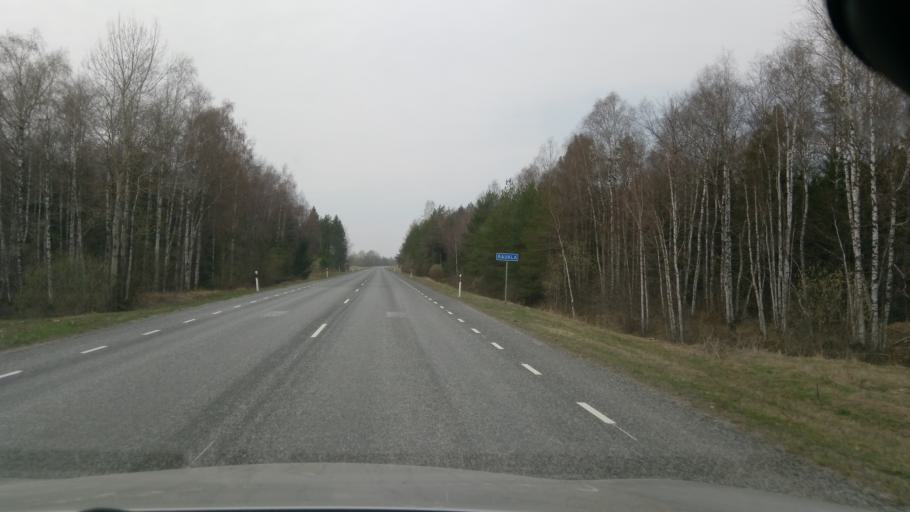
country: EE
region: Jaervamaa
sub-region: Tueri vald
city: Sarevere
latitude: 58.7649
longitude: 25.5389
